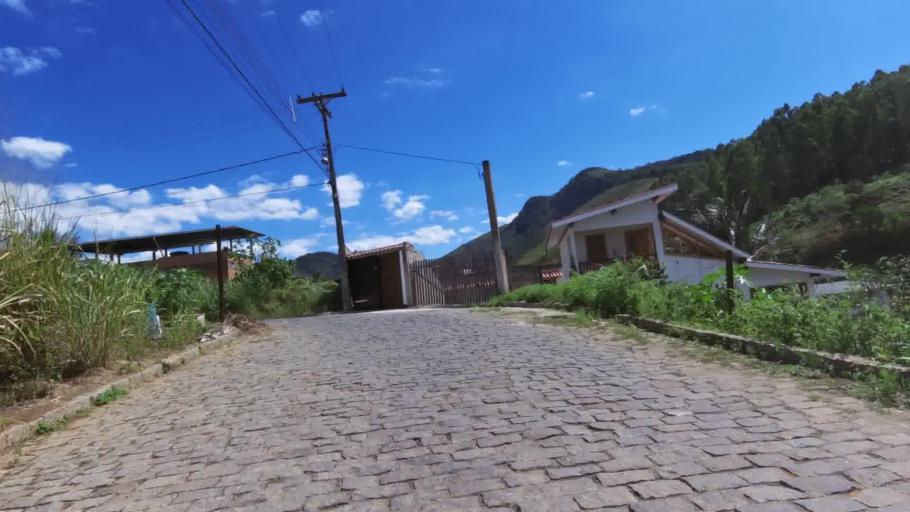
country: BR
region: Espirito Santo
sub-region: Rio Novo Do Sul
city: Rio Novo do Sul
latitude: -20.8652
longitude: -40.9420
